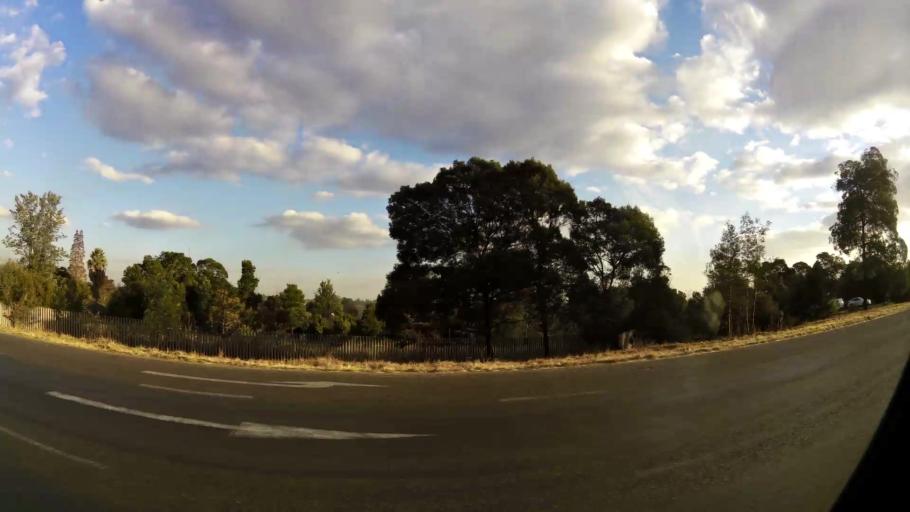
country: ZA
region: Gauteng
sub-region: City of Johannesburg Metropolitan Municipality
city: Midrand
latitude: -25.9469
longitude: 28.1551
